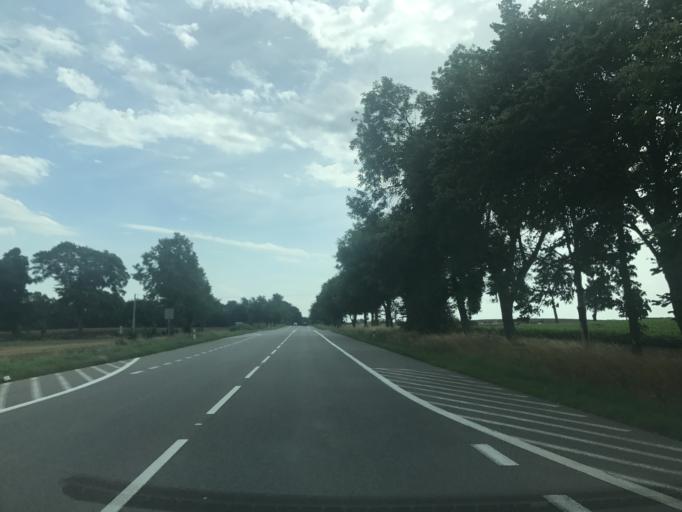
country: PL
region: Warmian-Masurian Voivodeship
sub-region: Powiat ostrodzki
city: Gierzwald
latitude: 53.6325
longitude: 20.0596
